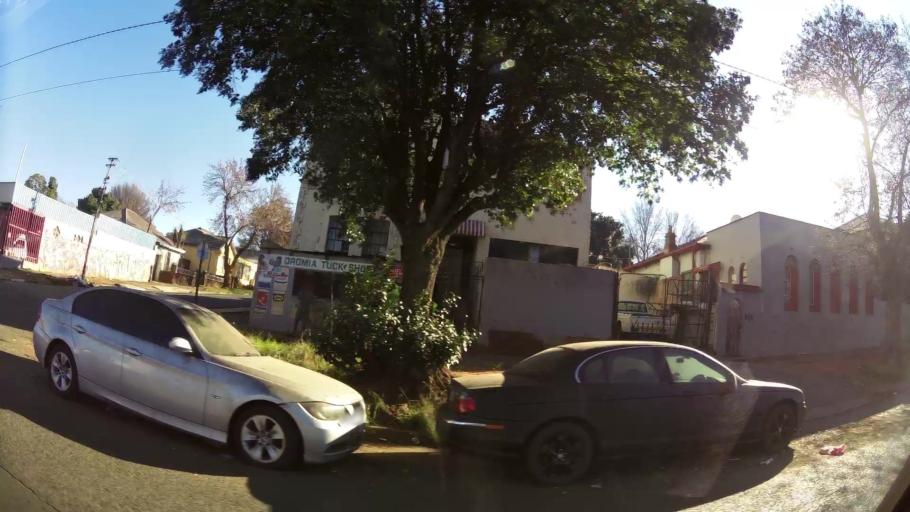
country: ZA
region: Gauteng
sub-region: City of Johannesburg Metropolitan Municipality
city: Johannesburg
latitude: -26.2044
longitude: 28.0883
